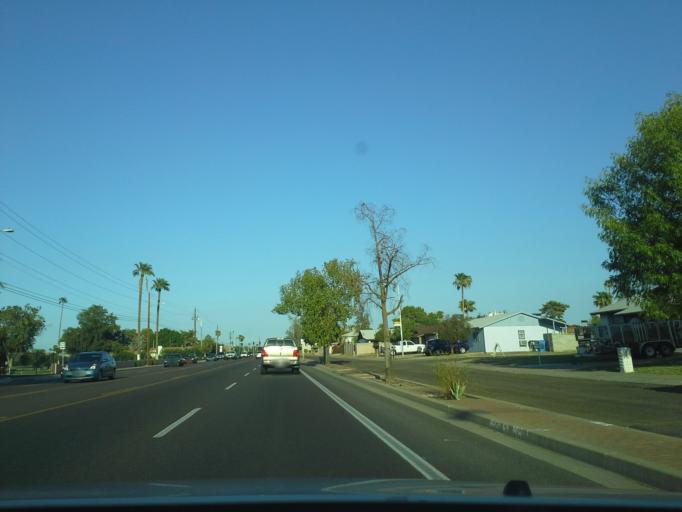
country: US
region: Arizona
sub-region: Maricopa County
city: Guadalupe
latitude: 33.3926
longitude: -111.9897
